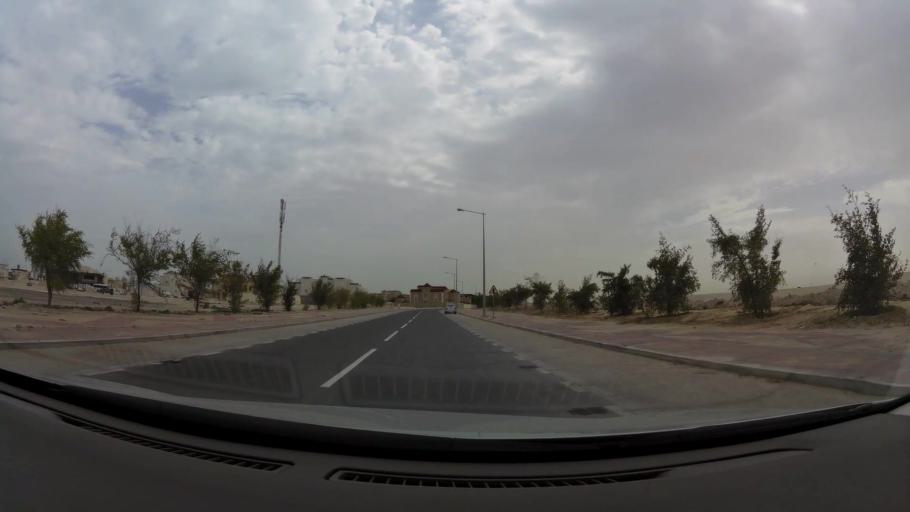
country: QA
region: Baladiyat ad Dawhah
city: Doha
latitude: 25.3571
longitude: 51.4936
